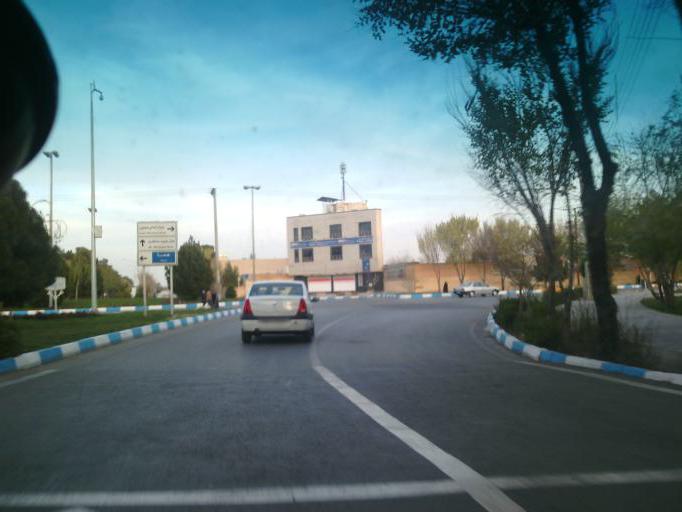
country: IR
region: Isfahan
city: Shahin Shahr
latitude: 32.8751
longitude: 51.5534
